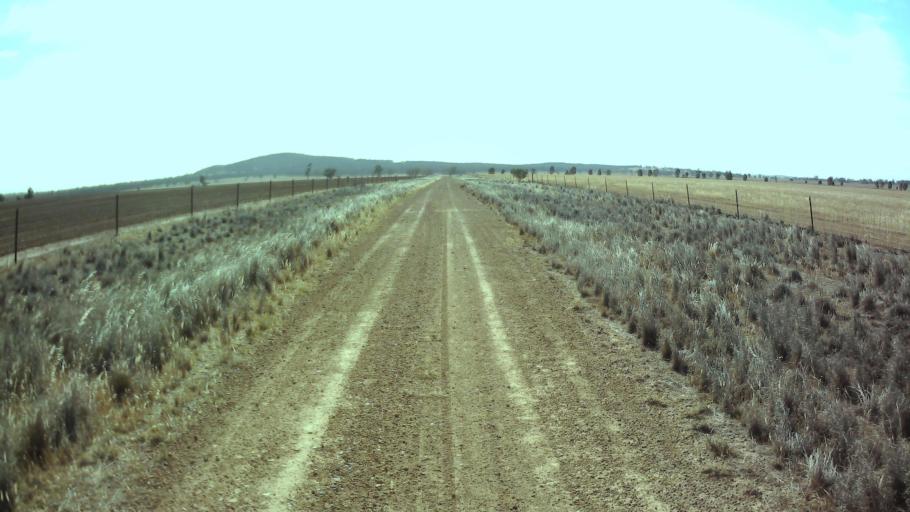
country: AU
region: New South Wales
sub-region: Weddin
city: Grenfell
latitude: -33.7329
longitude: 148.0011
